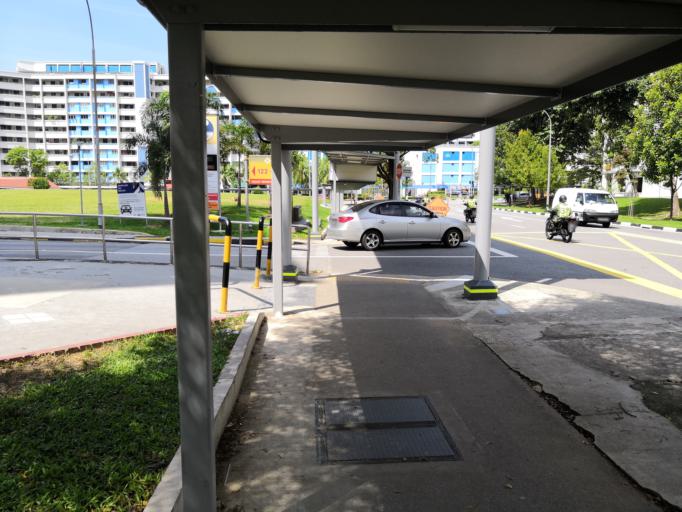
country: SG
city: Singapore
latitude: 1.3325
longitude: 103.9095
